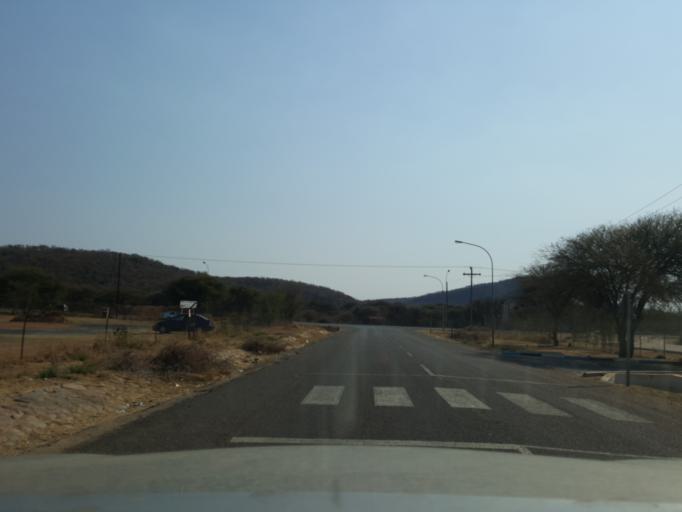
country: BW
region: South East
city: Lobatse
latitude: -25.1860
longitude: 25.6946
